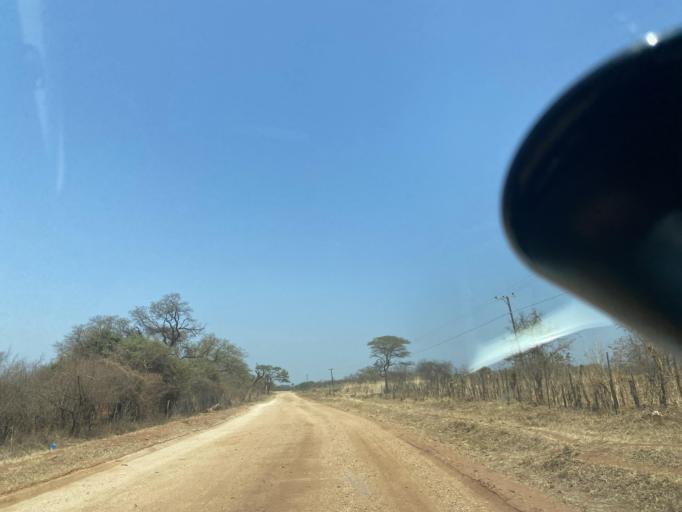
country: ZM
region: Lusaka
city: Lusaka
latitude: -15.5401
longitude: 28.0777
